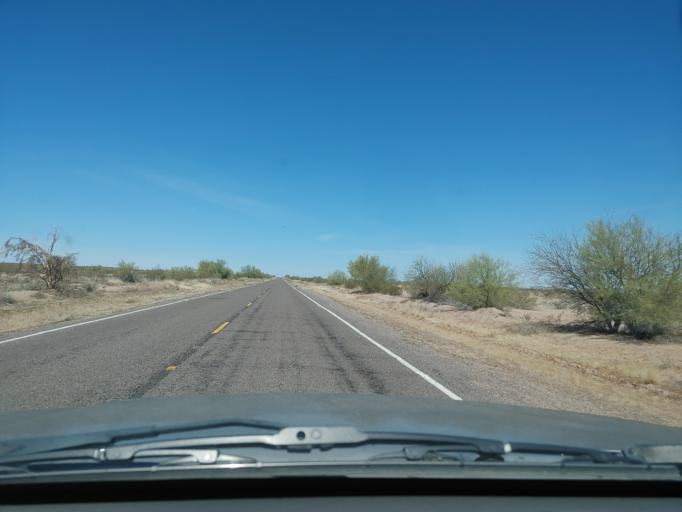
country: US
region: Arizona
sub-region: Maricopa County
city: Gila Bend
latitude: 32.8783
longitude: -113.2227
